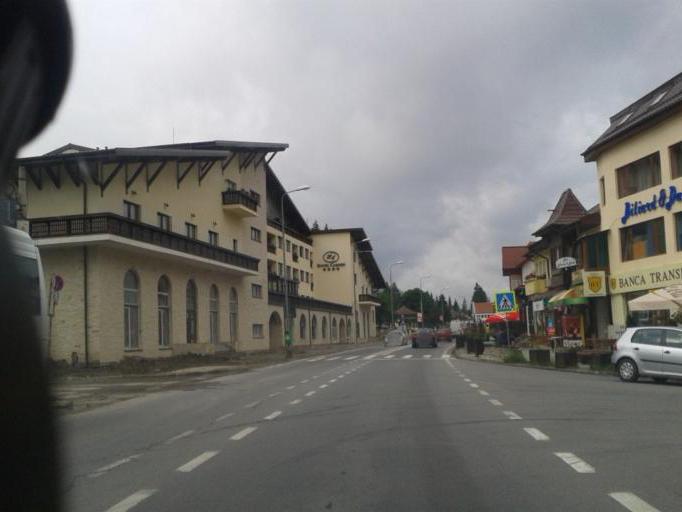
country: RO
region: Brasov
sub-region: Oras Predeal
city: Predeal
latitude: 45.5040
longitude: 25.5739
